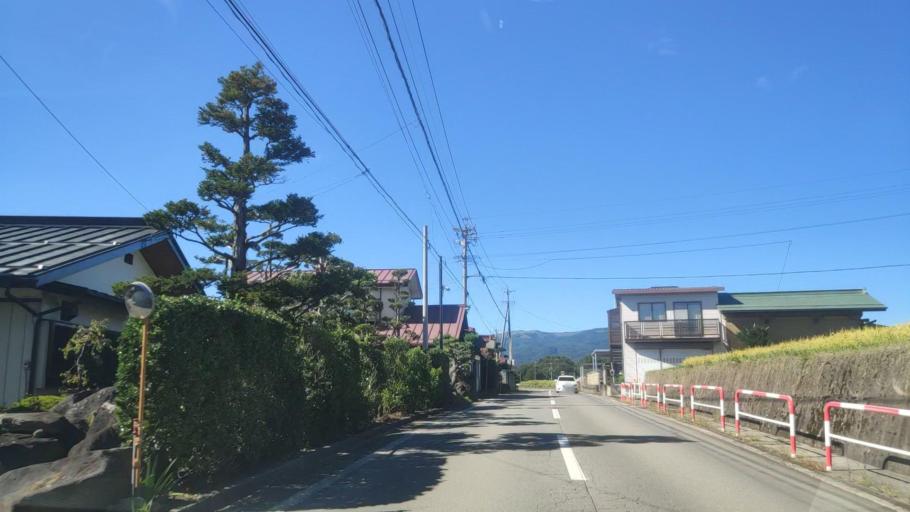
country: JP
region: Nagano
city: Chino
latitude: 36.0050
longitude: 138.2093
